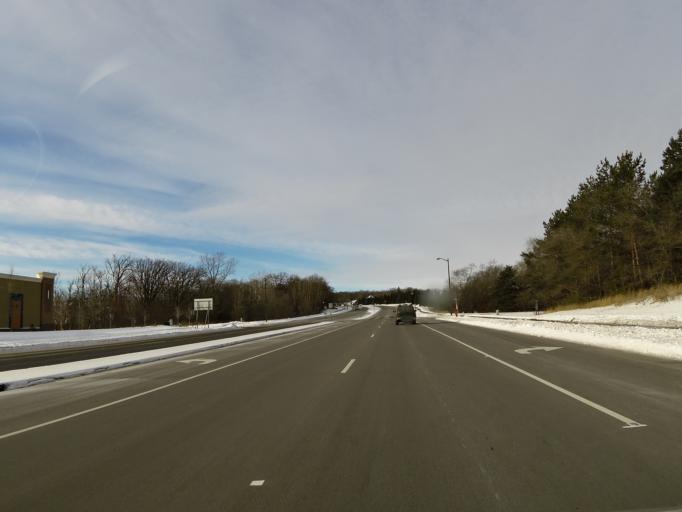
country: US
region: Minnesota
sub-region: Dakota County
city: Burnsville
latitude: 44.7151
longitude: -93.2904
